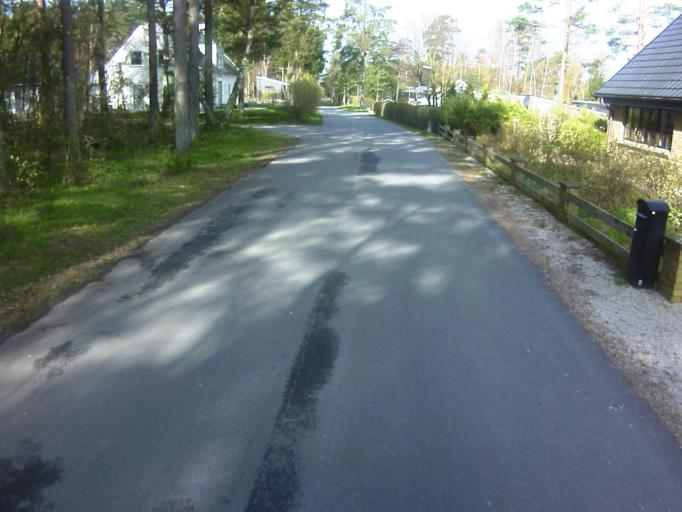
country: SE
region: Skane
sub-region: Kavlinge Kommun
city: Hofterup
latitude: 55.7990
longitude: 12.9808
